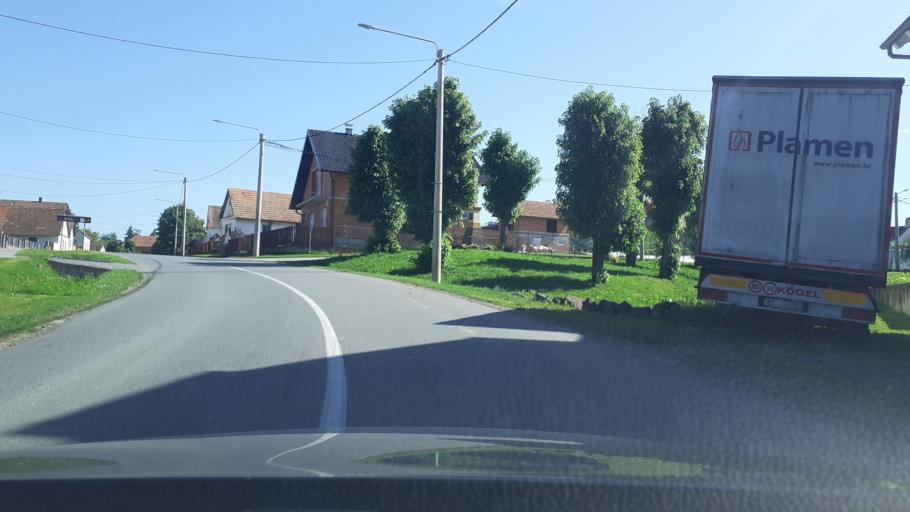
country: HR
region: Pozesko-Slavonska
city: Jaksic
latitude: 45.3519
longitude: 17.7607
